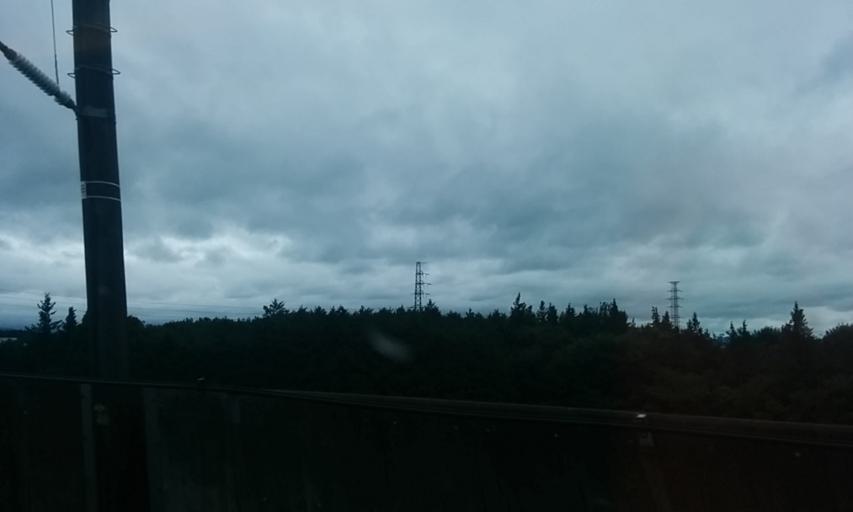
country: JP
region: Tochigi
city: Kuroiso
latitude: 36.9441
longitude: 140.0337
